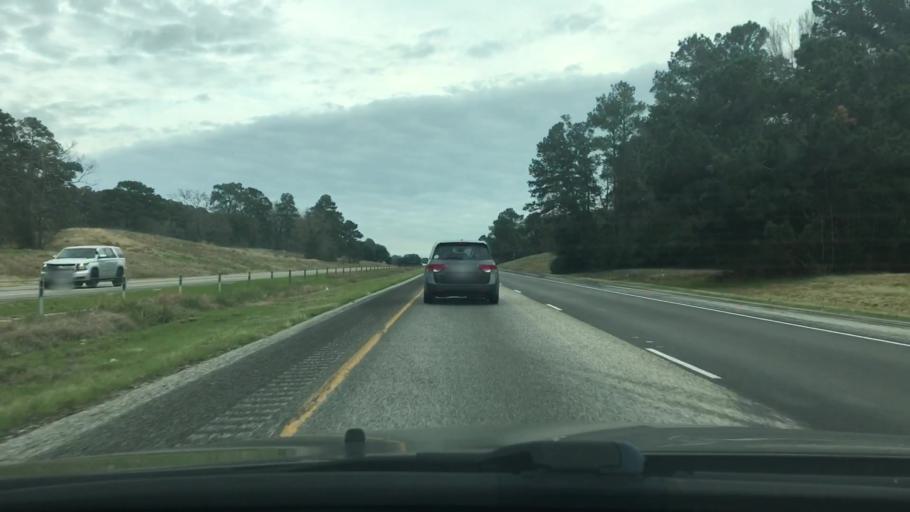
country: US
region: Texas
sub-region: Walker County
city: Huntsville
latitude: 30.8196
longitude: -95.7019
